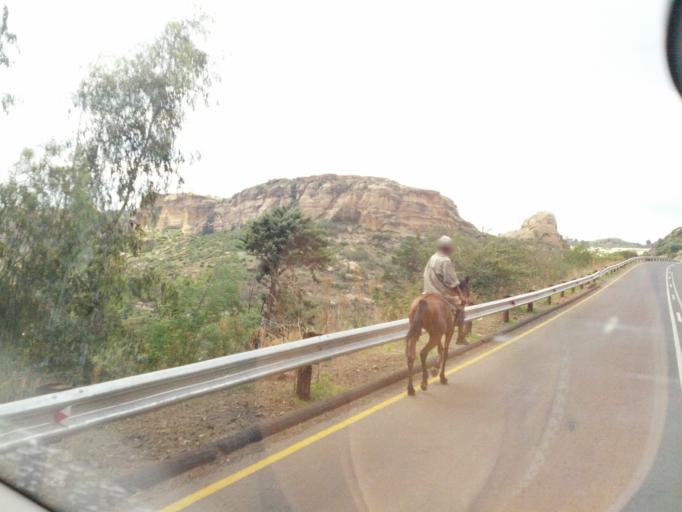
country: LS
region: Maseru
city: Nako
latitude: -29.4775
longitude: 27.7387
